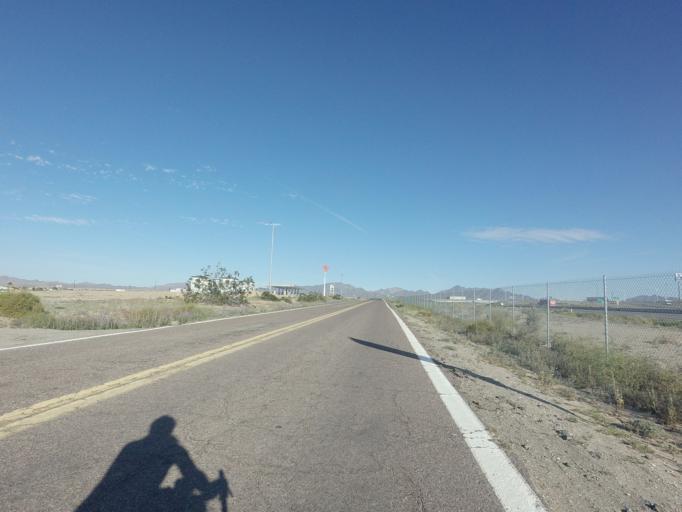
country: US
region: Arizona
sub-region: La Paz County
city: Ehrenberg
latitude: 33.6034
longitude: -114.5233
